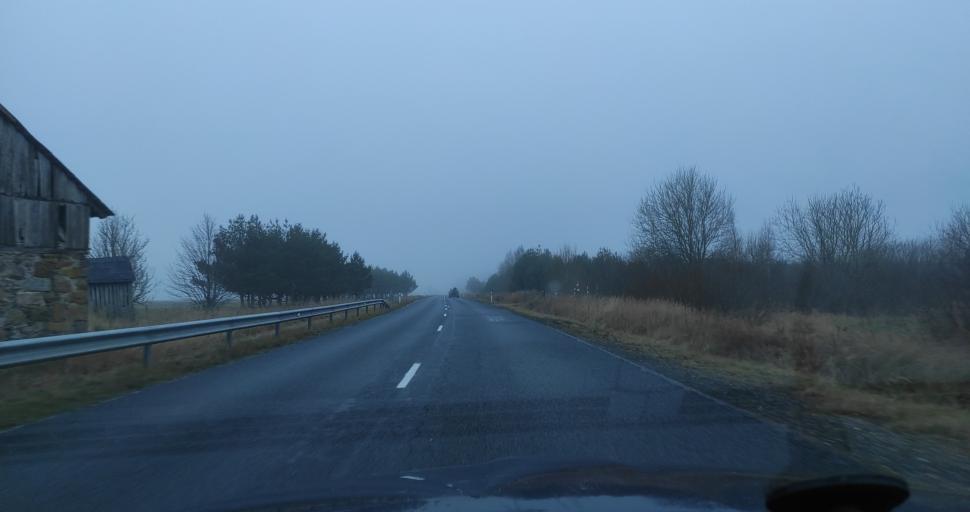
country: LV
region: Alsunga
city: Alsunga
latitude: 57.1130
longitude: 21.4229
